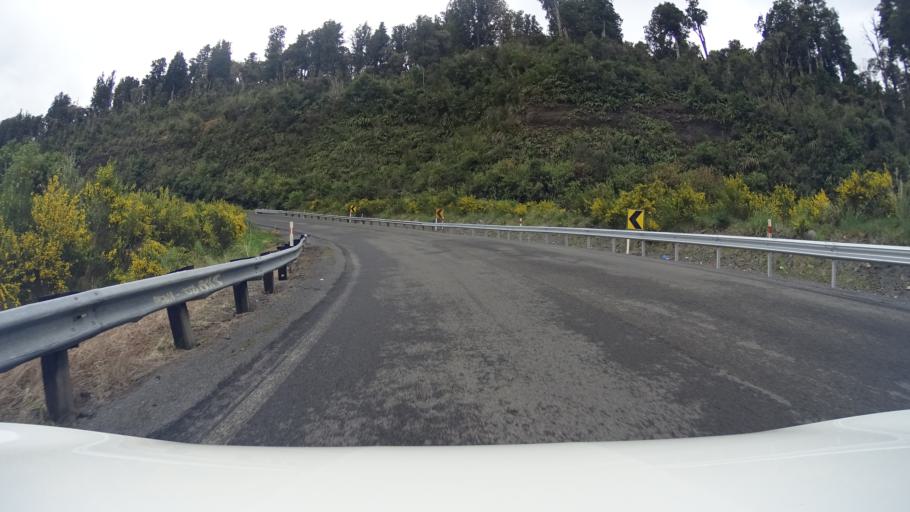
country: NZ
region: Manawatu-Wanganui
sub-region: Ruapehu District
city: Waiouru
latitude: -39.2645
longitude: 175.3989
